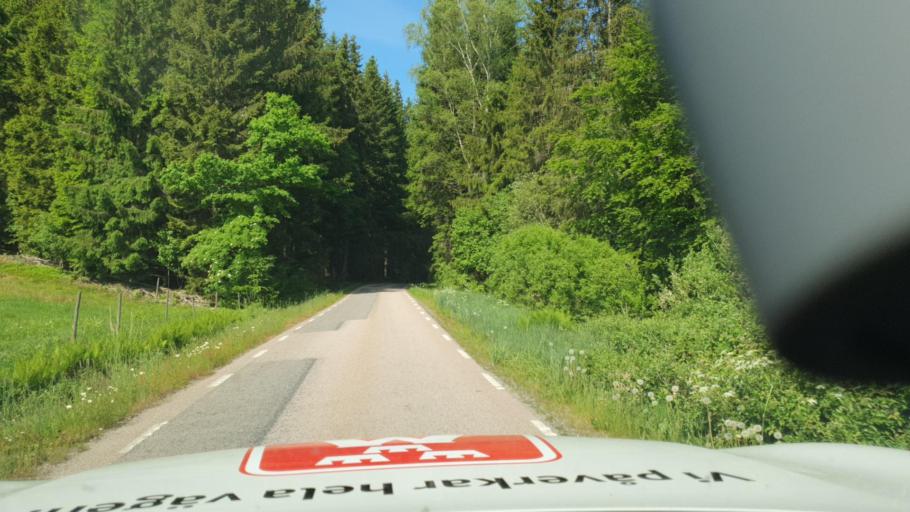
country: SE
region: Vaestra Goetaland
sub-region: Herrljunga Kommun
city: Herrljunga
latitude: 57.9216
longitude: 13.1369
